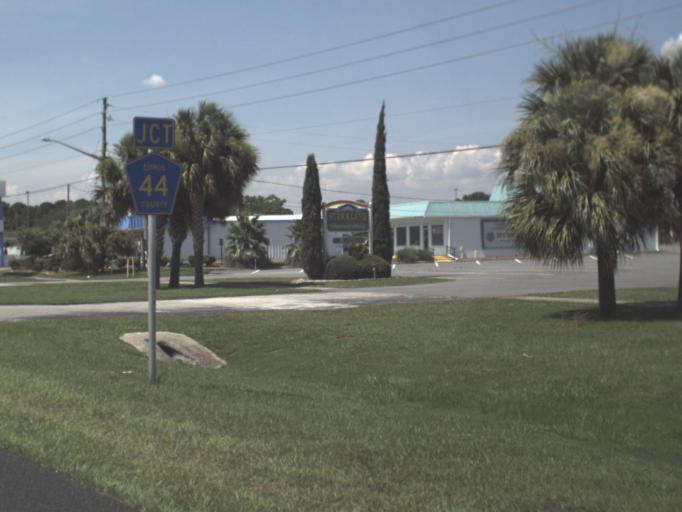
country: US
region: Florida
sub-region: Citrus County
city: Crystal River
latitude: 28.8809
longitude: -82.5819
